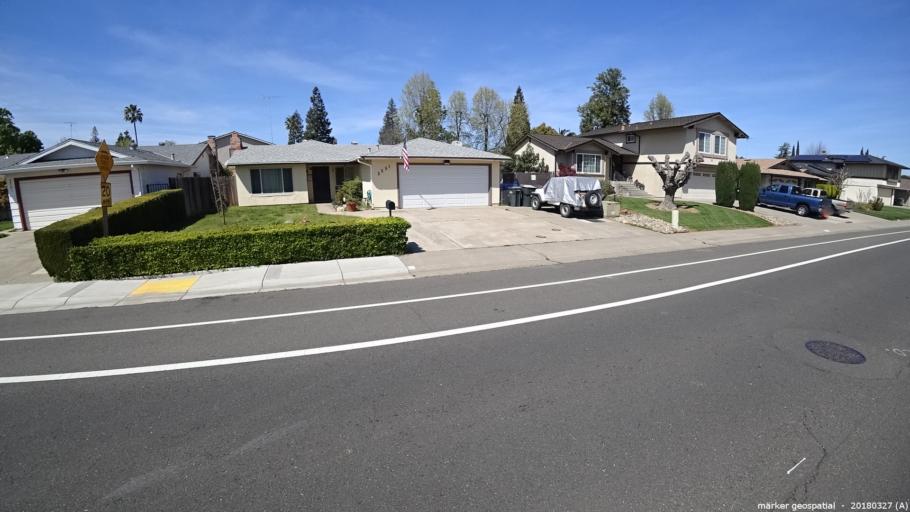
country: US
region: California
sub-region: Sacramento County
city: La Riviera
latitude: 38.5570
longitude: -121.3536
